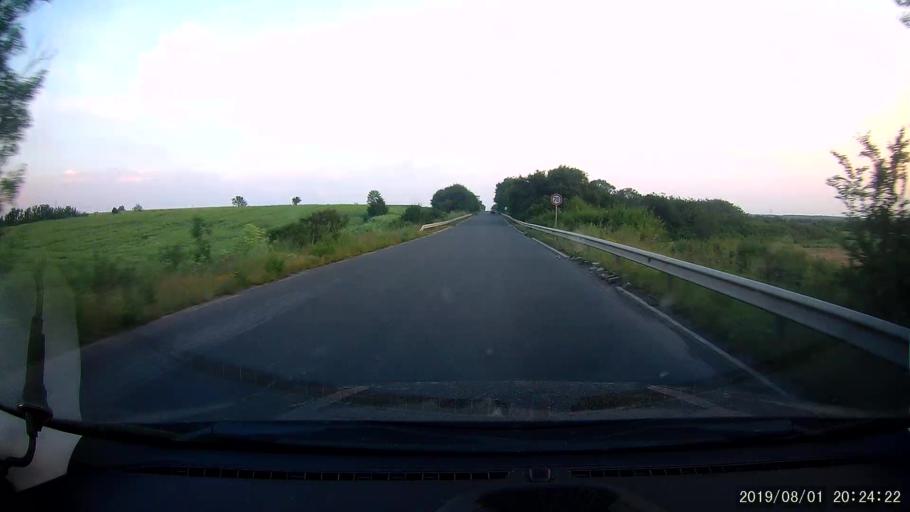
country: BG
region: Yambol
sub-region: Obshtina Elkhovo
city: Elkhovo
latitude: 42.2329
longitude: 26.5940
